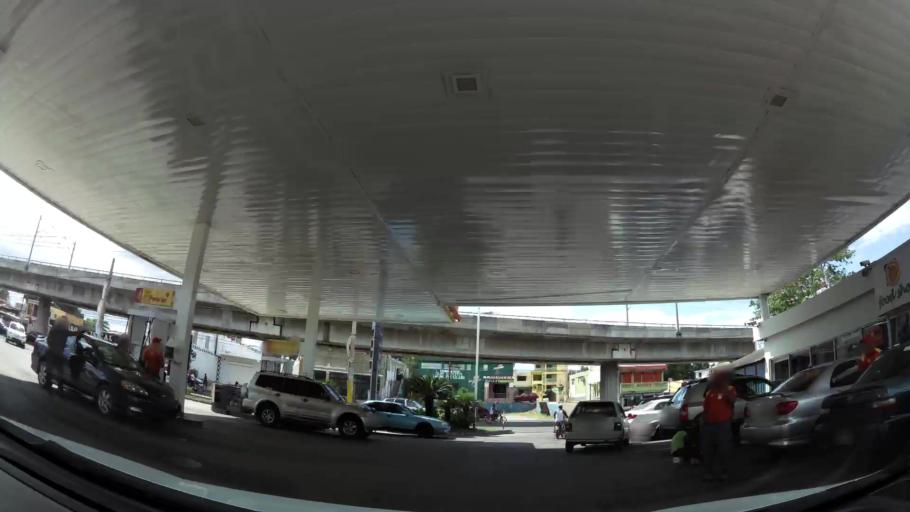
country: DO
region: Nacional
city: Ensanche Luperon
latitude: 18.5325
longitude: -69.9065
